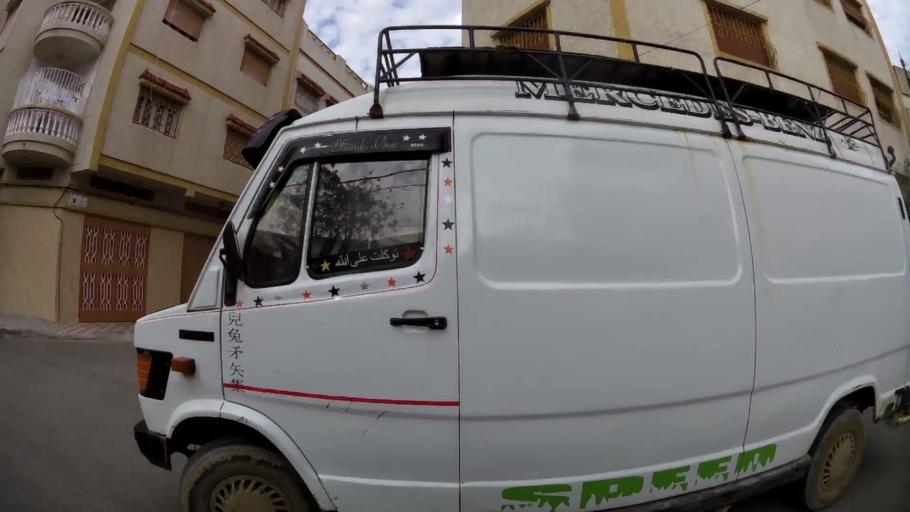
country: MA
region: Tanger-Tetouan
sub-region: Tanger-Assilah
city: Tangier
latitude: 35.7574
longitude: -5.7947
